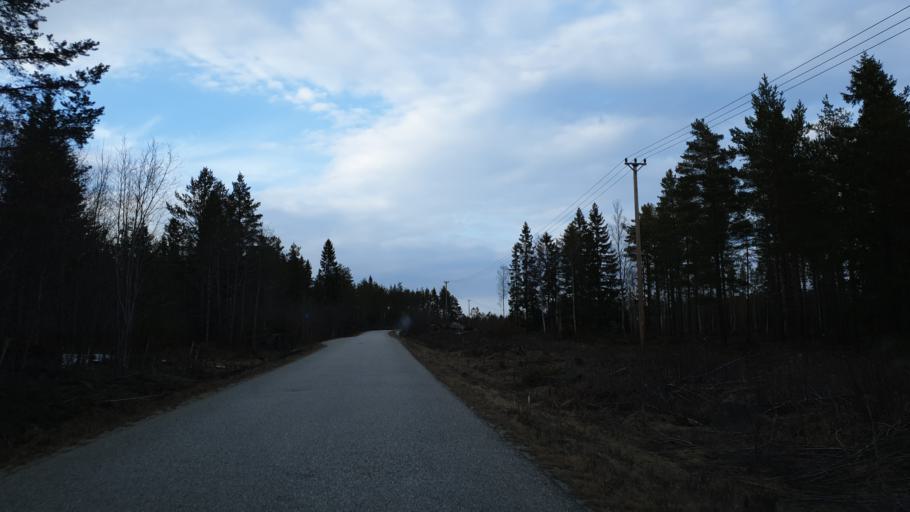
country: SE
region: Vaesternorrland
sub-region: Sundsvalls Kommun
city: Njurundabommen
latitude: 62.0042
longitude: 17.3909
